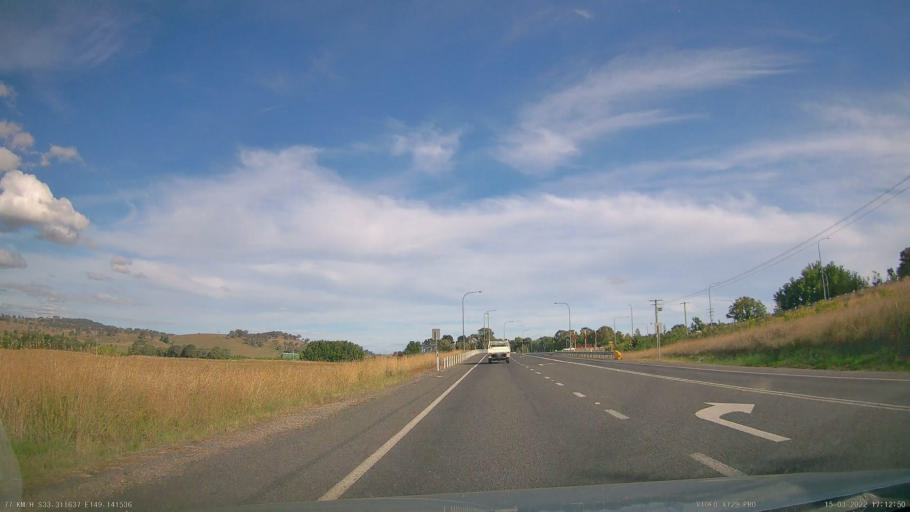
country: AU
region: New South Wales
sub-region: Orange Municipality
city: Orange
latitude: -33.3116
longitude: 149.1416
